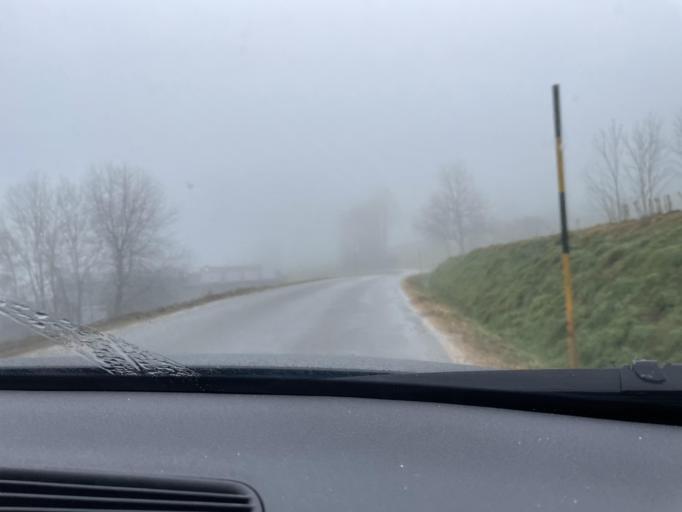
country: DE
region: Bavaria
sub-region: Lower Bavaria
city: Ruhmannsfelden
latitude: 48.9983
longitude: 13.0143
